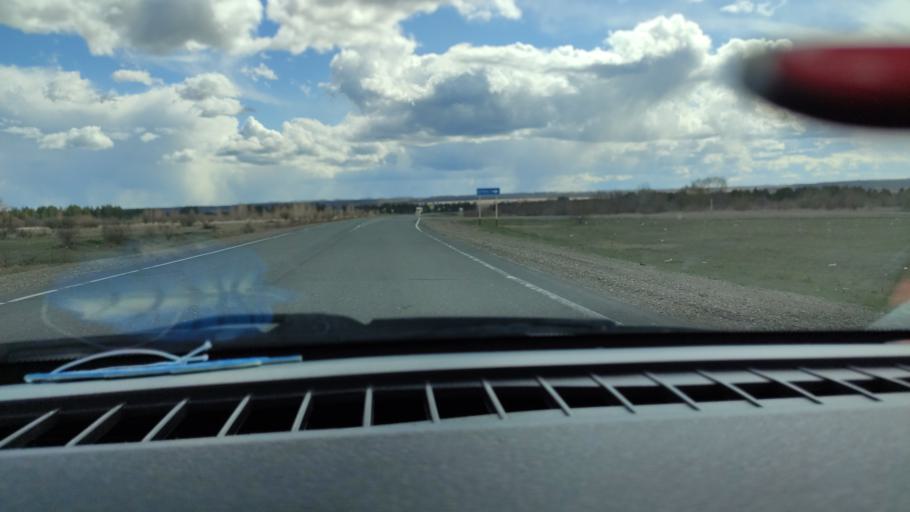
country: RU
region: Samara
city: Varlamovo
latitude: 53.1547
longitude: 48.2846
